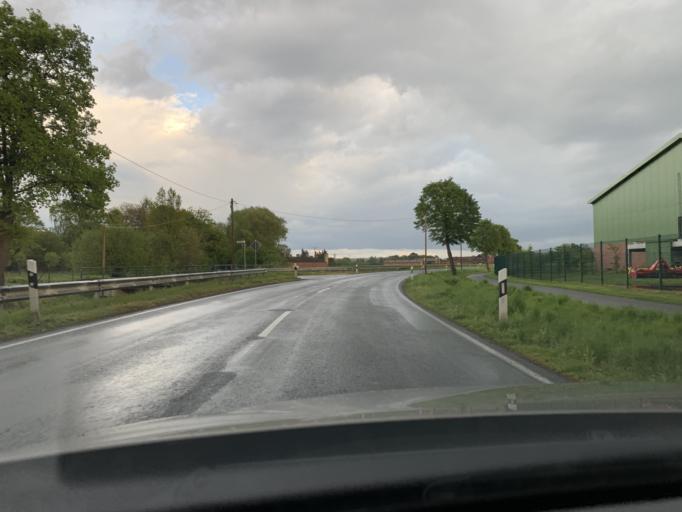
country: DE
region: North Rhine-Westphalia
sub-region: Regierungsbezirk Detmold
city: Langenberg
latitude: 51.7964
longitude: 8.3697
